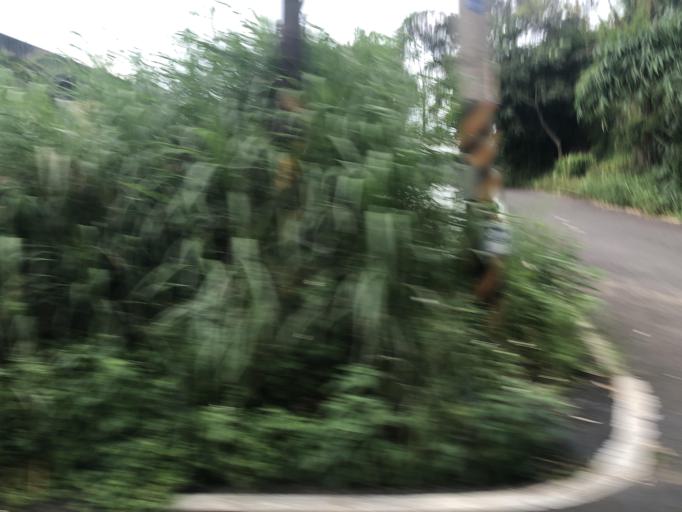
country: TW
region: Taiwan
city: Daxi
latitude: 24.9200
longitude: 121.3585
